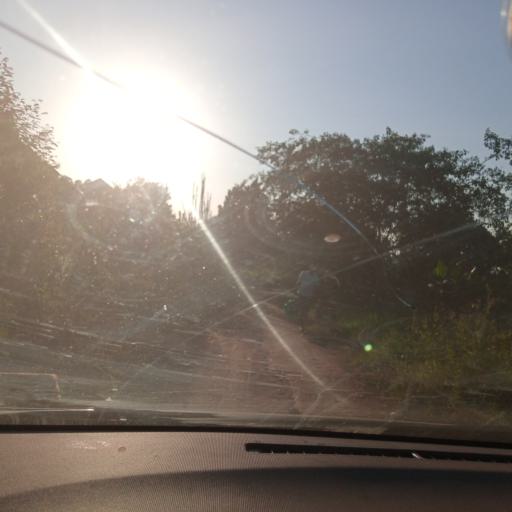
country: UG
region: Central Region
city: Masaka
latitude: -0.3412
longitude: 31.7582
